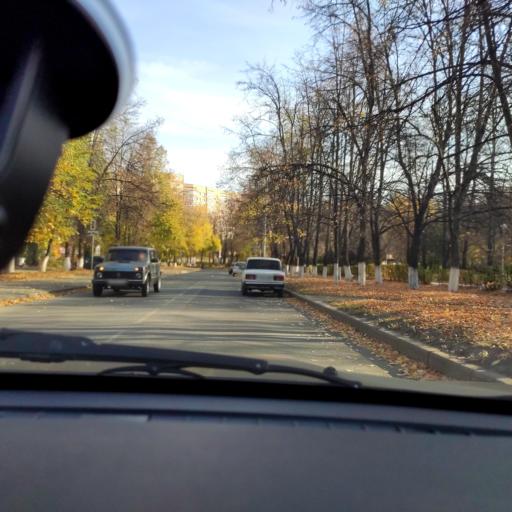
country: RU
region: Samara
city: Tol'yatti
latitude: 53.5136
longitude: 49.2664
